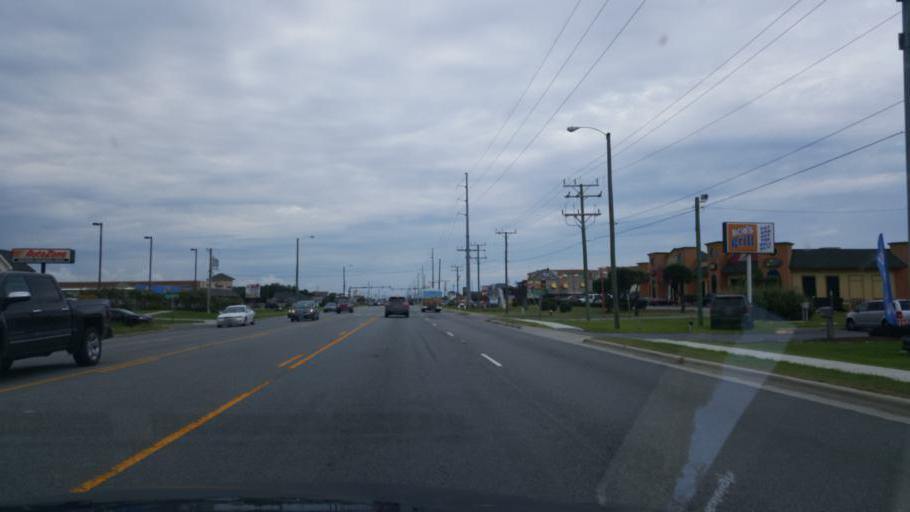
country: US
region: North Carolina
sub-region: Dare County
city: Kill Devil Hills
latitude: 36.0021
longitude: -75.6540
